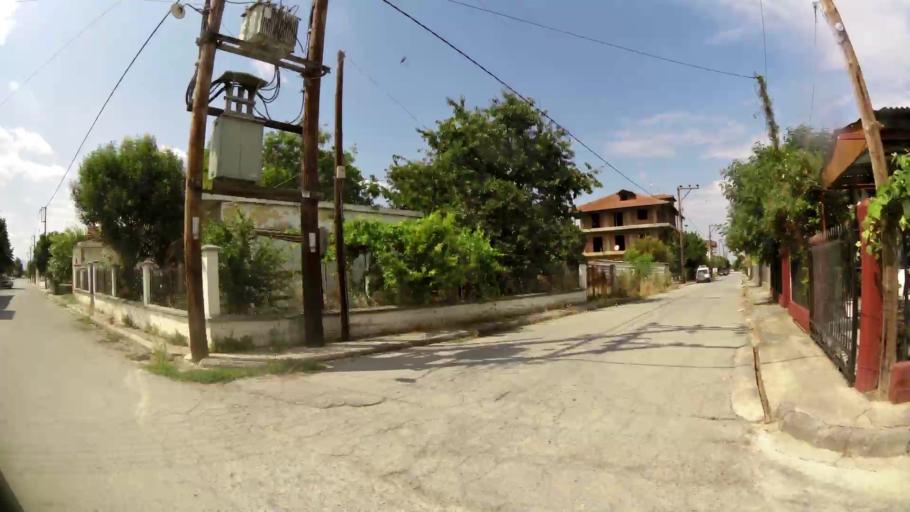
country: GR
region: Central Macedonia
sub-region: Nomos Pierias
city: Korinos
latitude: 40.3187
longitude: 22.5860
